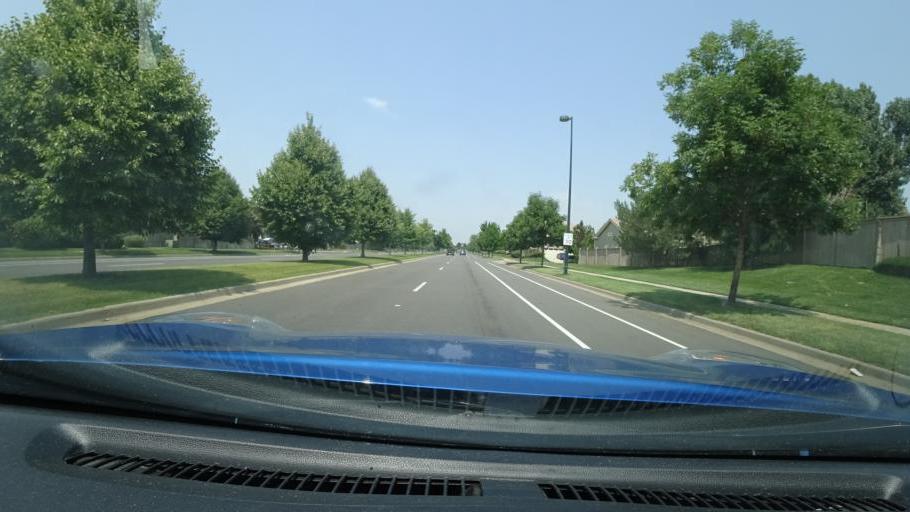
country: US
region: Colorado
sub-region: Adams County
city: Aurora
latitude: 39.7715
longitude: -104.7533
